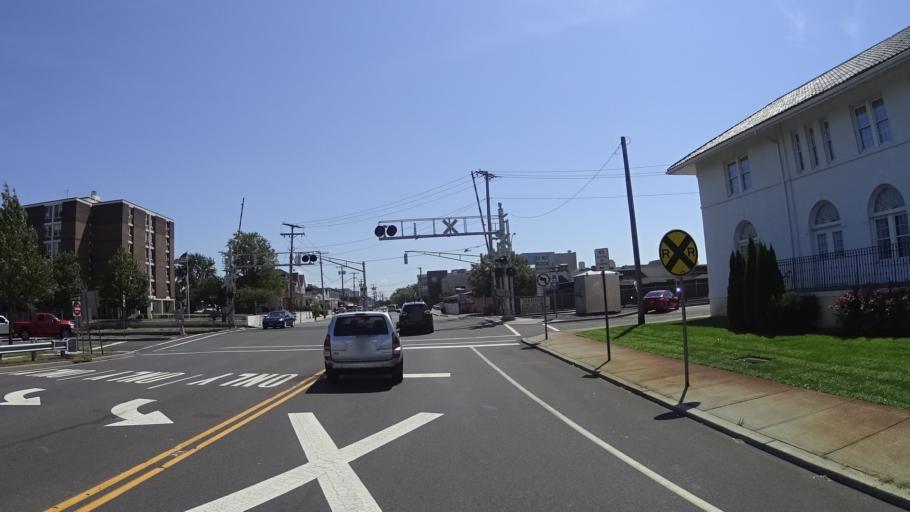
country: US
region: New Jersey
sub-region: Monmouth County
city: Belmar
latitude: 40.1819
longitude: -74.0274
